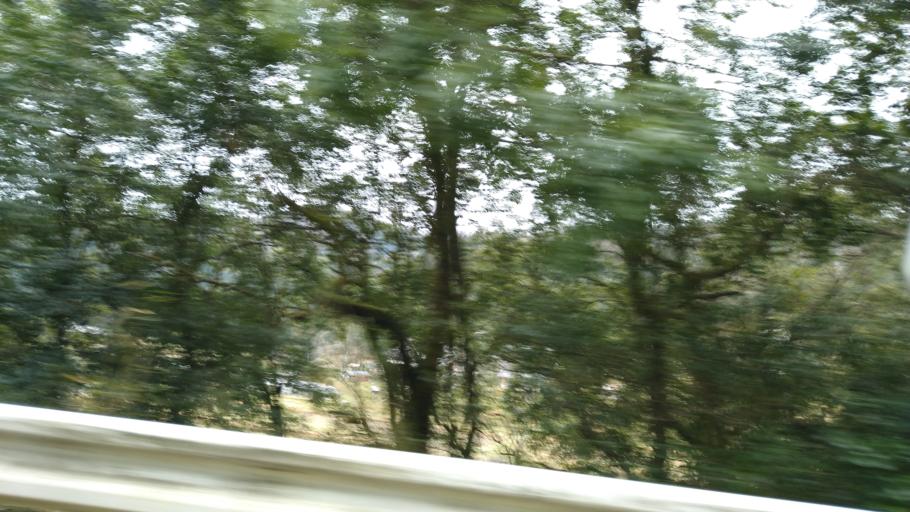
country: JP
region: Kyoto
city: Ayabe
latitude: 35.3302
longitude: 135.3521
